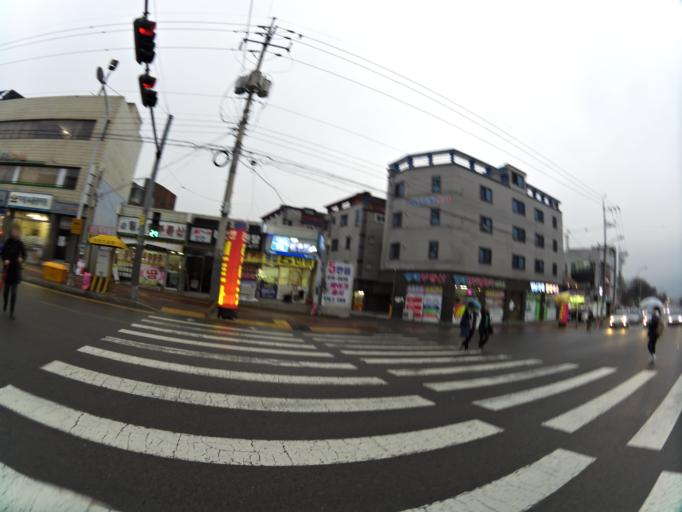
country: KR
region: Gyeongsangbuk-do
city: Gyeongsan-si
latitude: 35.8390
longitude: 128.7567
